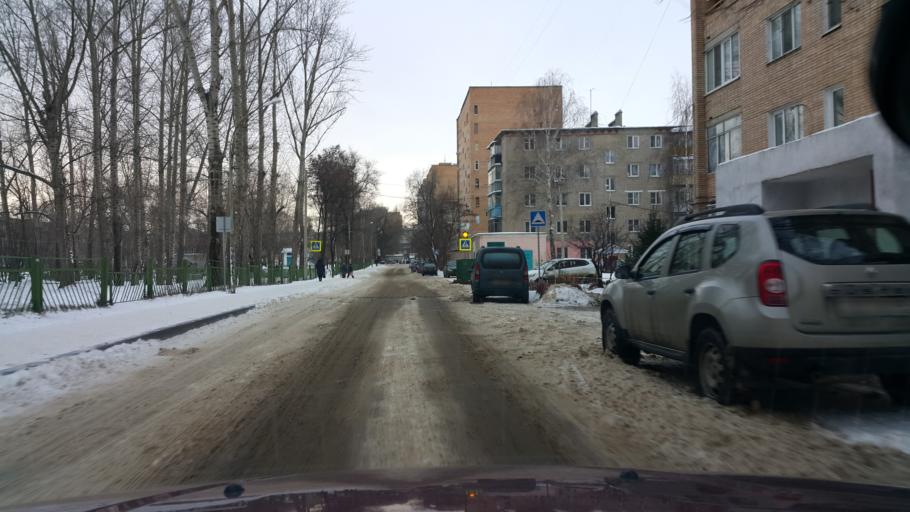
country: RU
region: Tambov
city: Bokino
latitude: 52.6538
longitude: 41.4487
